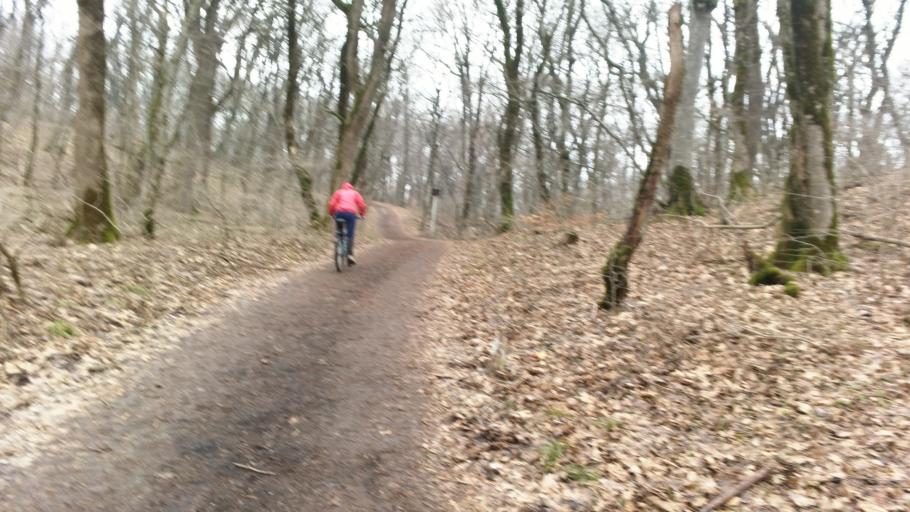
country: RU
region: Stavropol'skiy
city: Zheleznovodsk
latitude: 44.1470
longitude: 43.0375
